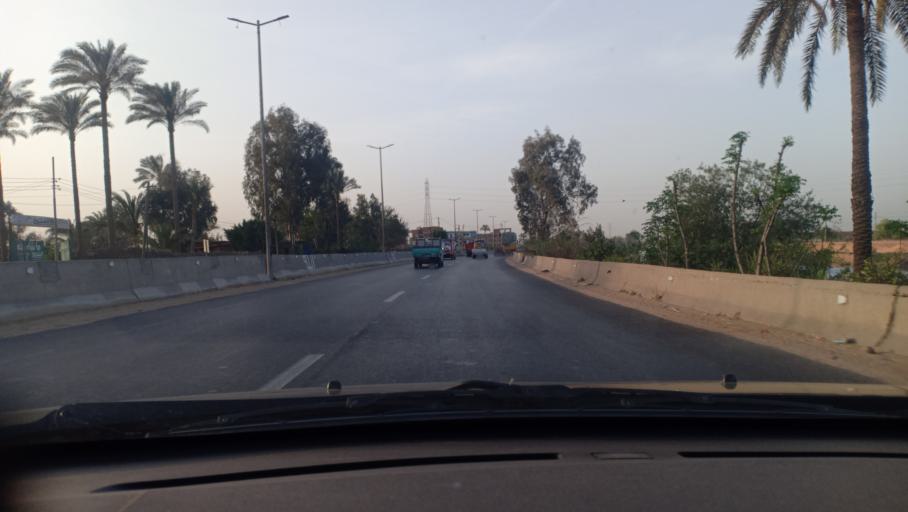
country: EG
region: Muhafazat al Minufiyah
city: Quwaysina
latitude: 30.5563
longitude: 31.2682
